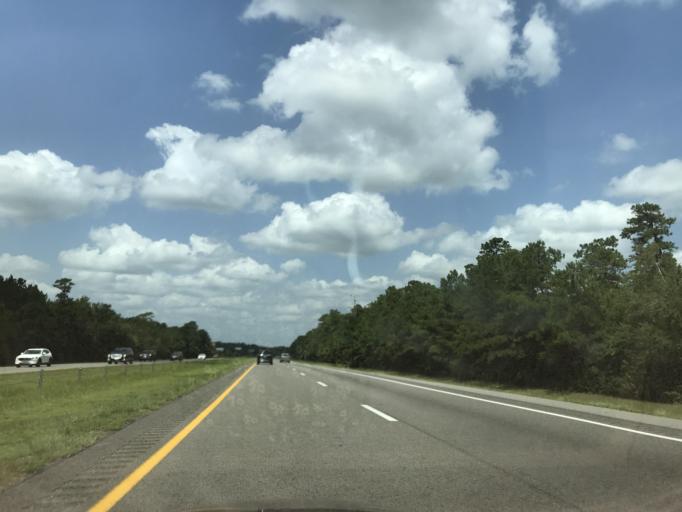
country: US
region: North Carolina
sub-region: Pender County
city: Burgaw
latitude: 34.5143
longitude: -77.8814
